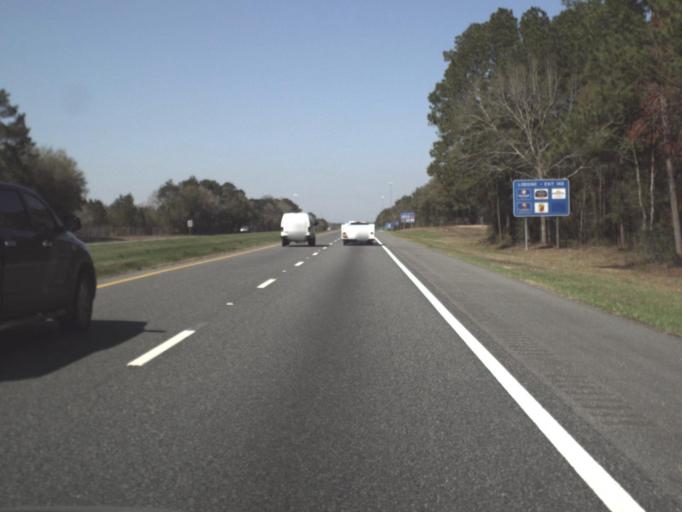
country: US
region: Florida
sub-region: Jackson County
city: Marianna
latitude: 30.7181
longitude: -85.1694
